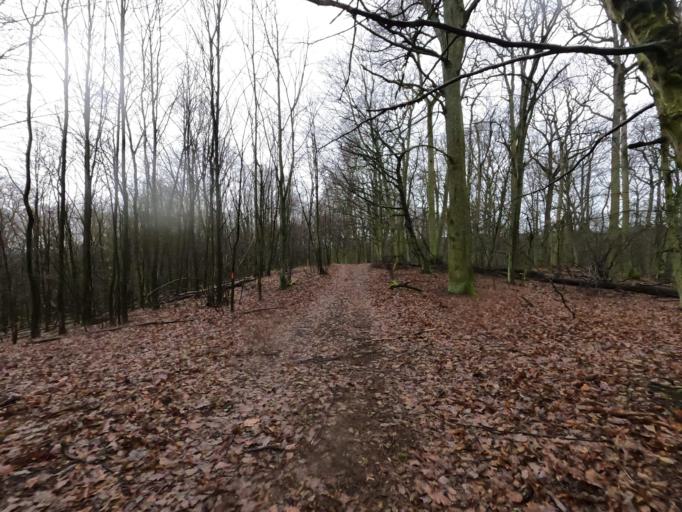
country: PL
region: Greater Poland Voivodeship
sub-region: Powiat pilski
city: Osiek nad Notecia
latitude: 53.1206
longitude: 17.2655
